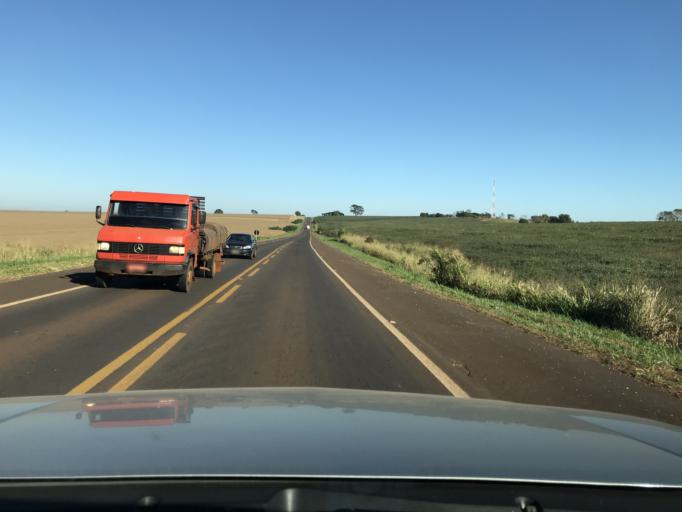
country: BR
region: Parana
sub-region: Ipora
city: Ipora
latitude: -24.0586
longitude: -53.8130
